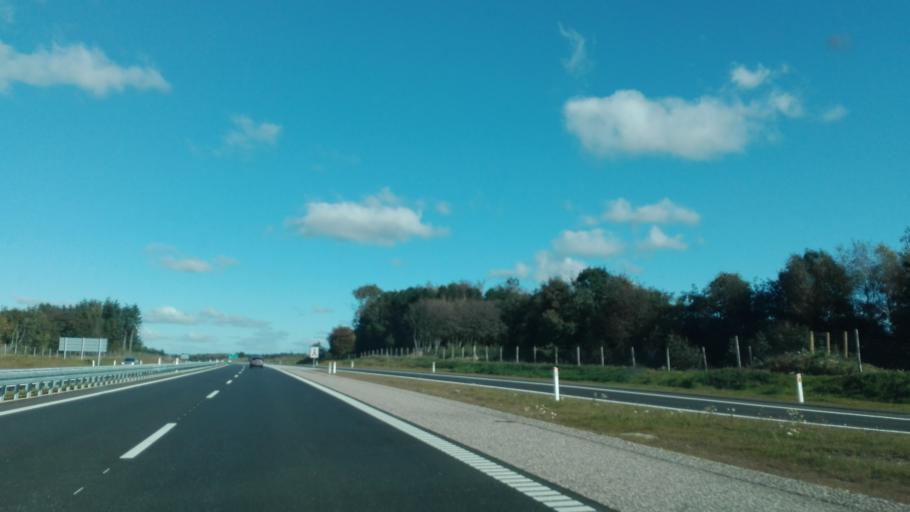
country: DK
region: Central Jutland
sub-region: Silkeborg Kommune
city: Silkeborg
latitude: 56.1549
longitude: 9.4579
